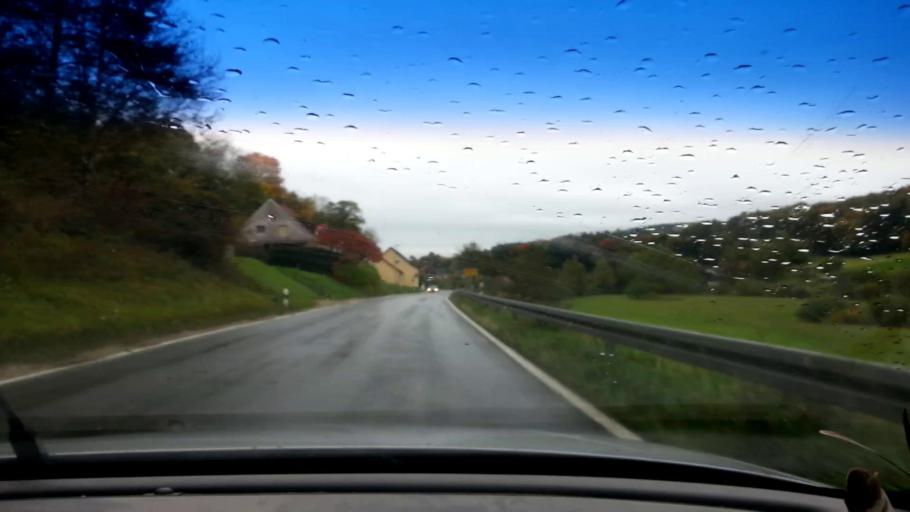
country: DE
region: Bavaria
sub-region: Upper Franconia
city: Heiligenstadt
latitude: 49.8722
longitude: 11.1512
